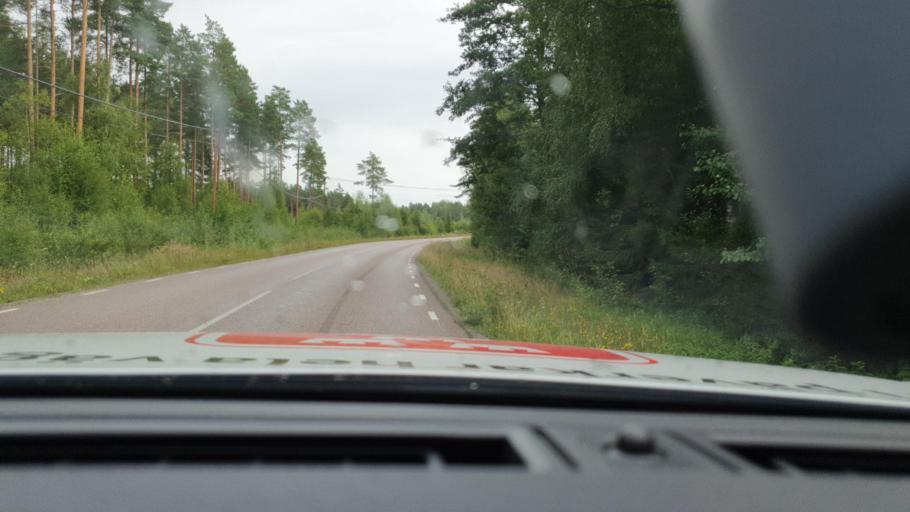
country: SE
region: Uppsala
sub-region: Heby Kommun
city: OEstervala
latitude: 60.0964
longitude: 17.1442
